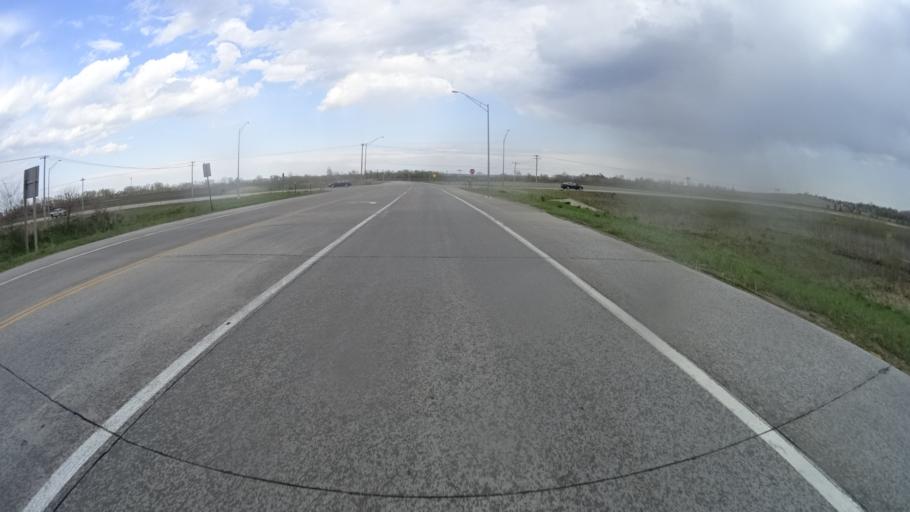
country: US
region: Nebraska
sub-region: Sarpy County
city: Offutt Air Force Base
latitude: 41.1037
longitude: -95.9275
